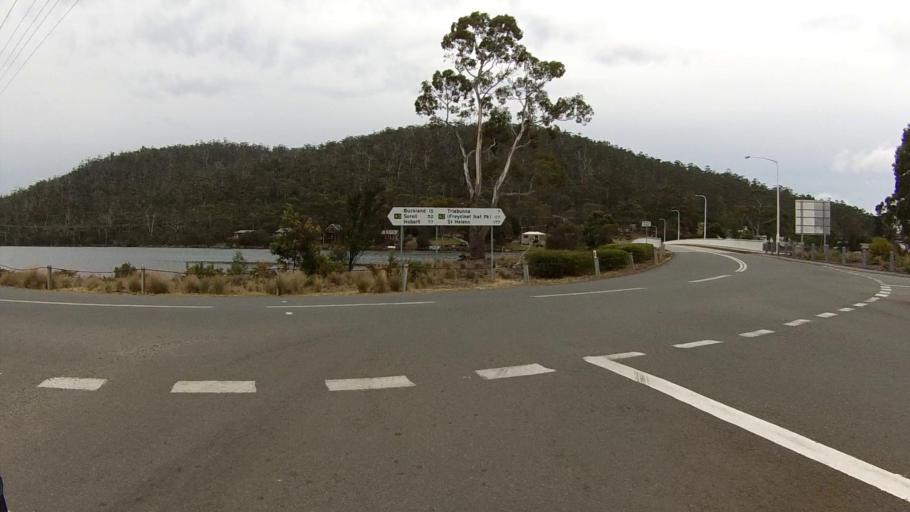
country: AU
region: Tasmania
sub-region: Sorell
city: Sorell
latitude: -42.5590
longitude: 147.8719
